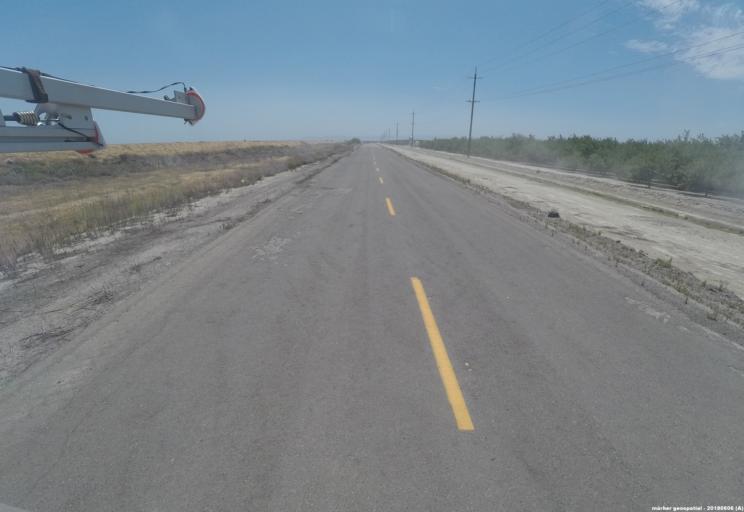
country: US
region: California
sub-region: Fresno County
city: Mendota
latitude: 36.7871
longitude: -120.3038
